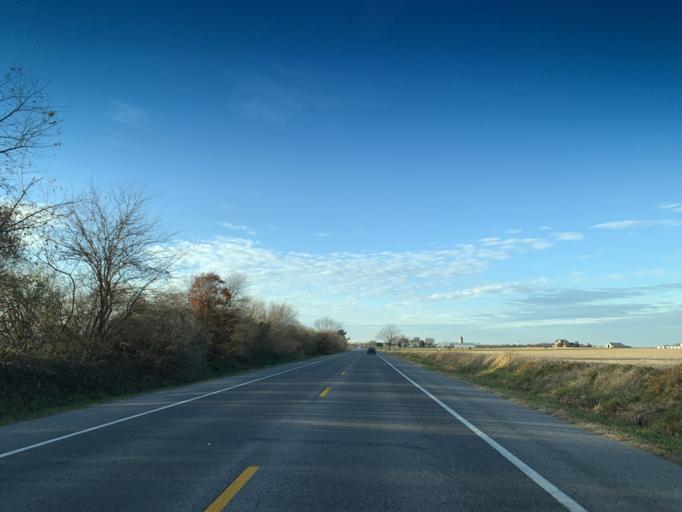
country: US
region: Maryland
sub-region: Kent County
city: Chestertown
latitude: 39.2549
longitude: -76.0800
